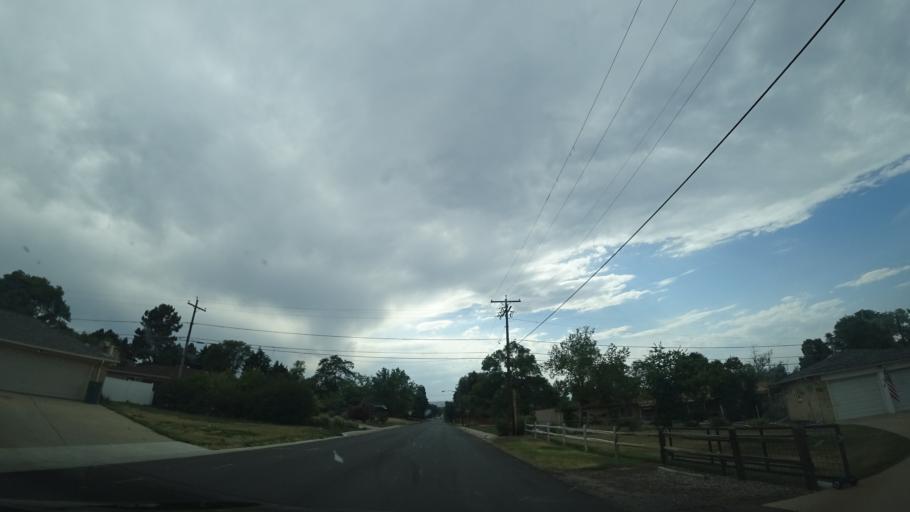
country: US
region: Colorado
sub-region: Jefferson County
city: Lakewood
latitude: 39.7148
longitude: -105.0864
